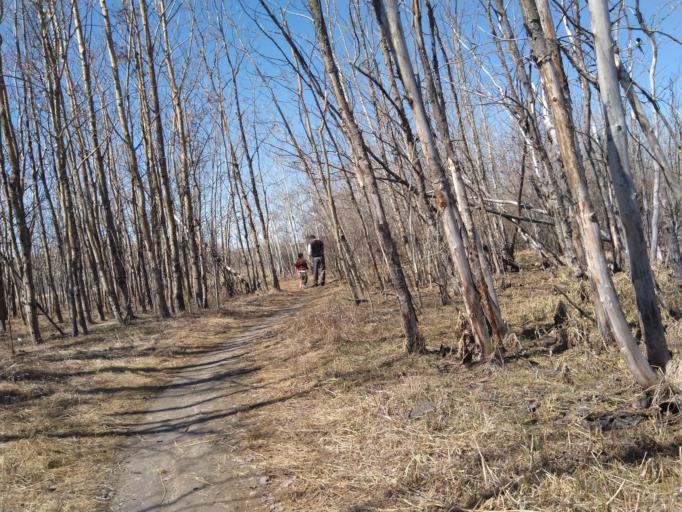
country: CA
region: Alberta
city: Chestermere
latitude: 51.0830
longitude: -113.9234
